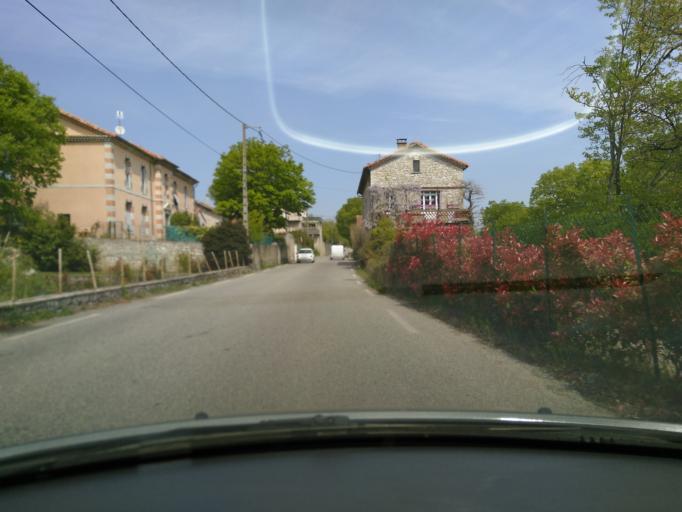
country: FR
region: Rhone-Alpes
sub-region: Departement de l'Ardeche
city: Saint-Sernin
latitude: 44.5410
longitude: 4.4152
